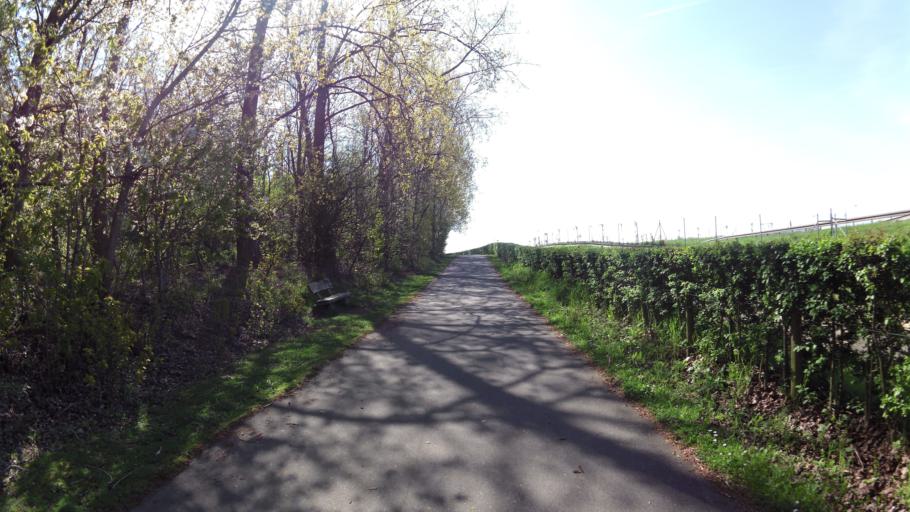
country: DE
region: North Rhine-Westphalia
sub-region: Regierungsbezirk Koln
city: Alsdorf
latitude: 50.9078
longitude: 6.1517
